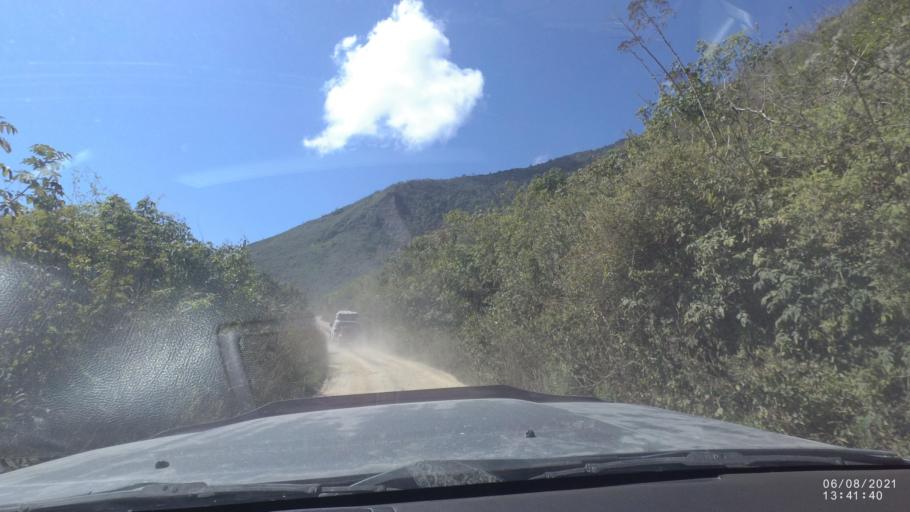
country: BO
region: La Paz
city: Quime
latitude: -16.6827
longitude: -66.7310
